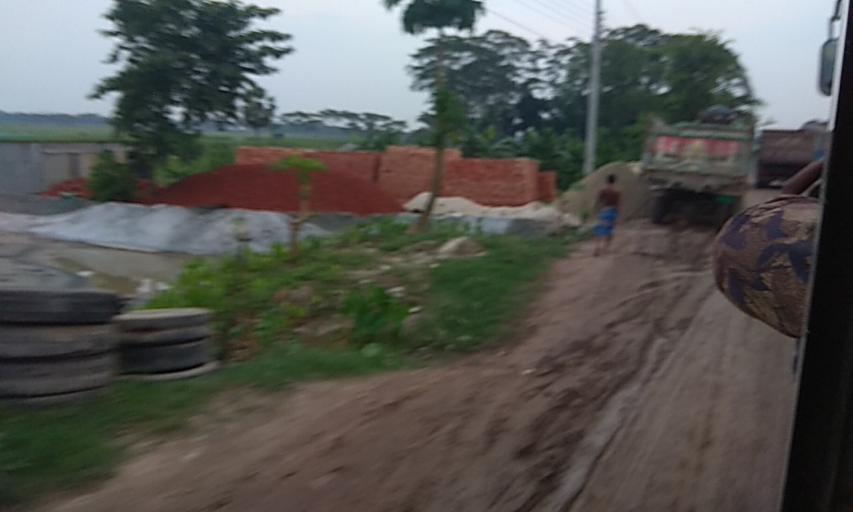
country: BD
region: Dhaka
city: Char Bhadrasan
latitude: 23.3867
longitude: 89.9921
